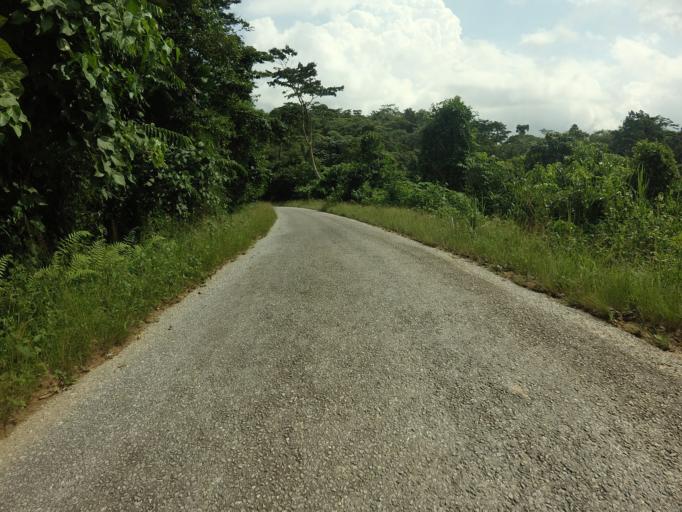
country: GH
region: Volta
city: Kpandu
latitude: 6.8333
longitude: 0.4241
